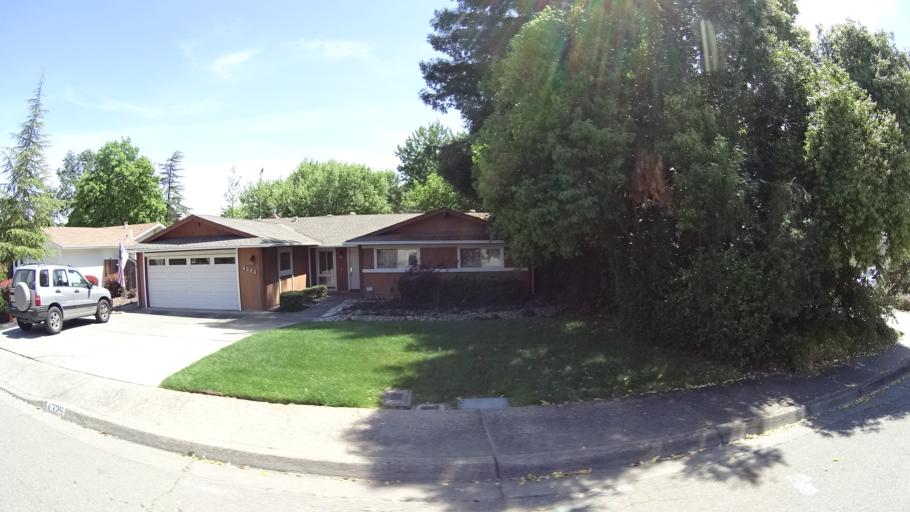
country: US
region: California
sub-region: Placer County
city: Rocklin
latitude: 38.8051
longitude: -121.2473
